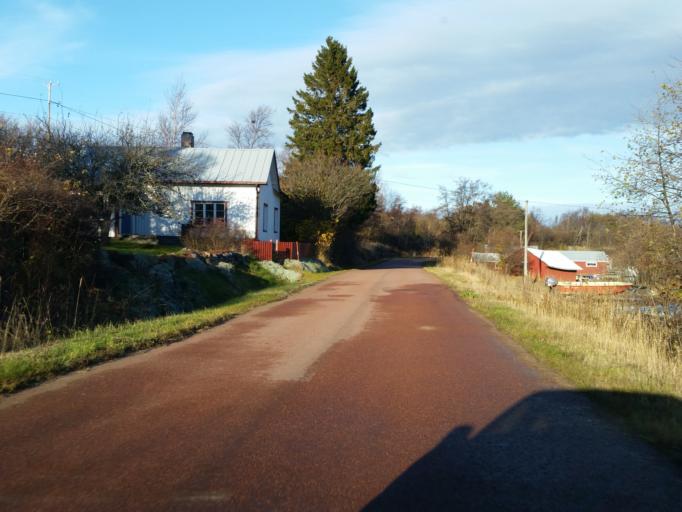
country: AX
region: Alands skaergard
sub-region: Kumlinge
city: Kumlinge
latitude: 60.2114
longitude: 20.7054
